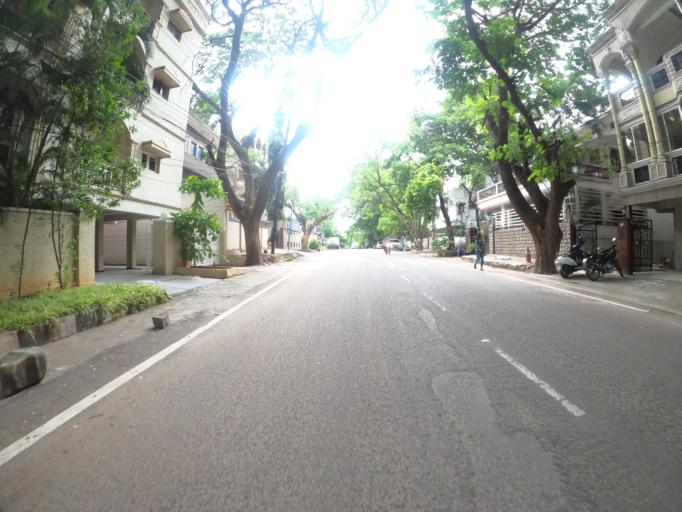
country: IN
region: Telangana
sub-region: Hyderabad
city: Hyderabad
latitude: 17.4218
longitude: 78.4082
